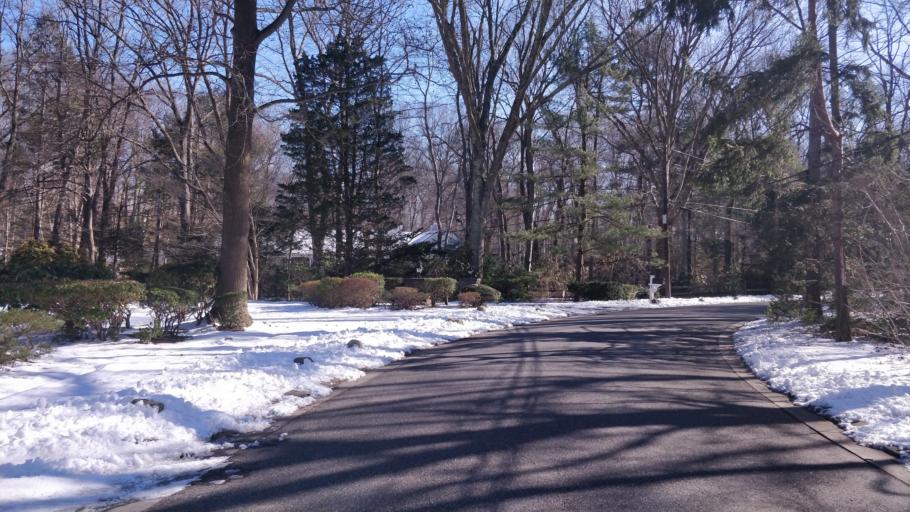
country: US
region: New York
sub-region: Nassau County
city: Old Brookville
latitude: 40.8493
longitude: -73.5931
